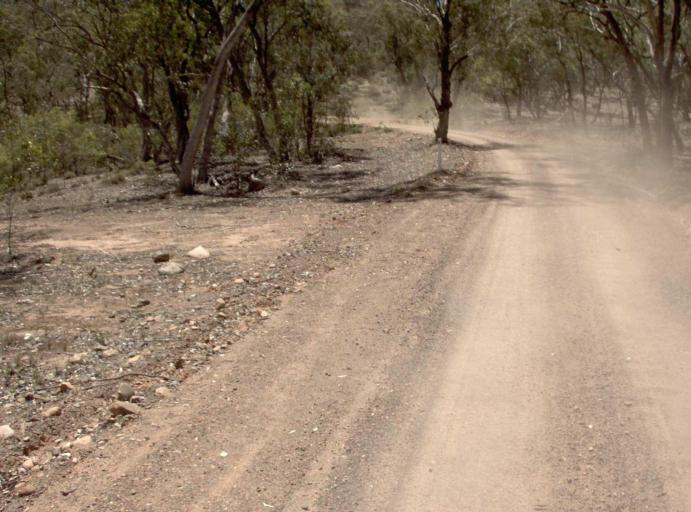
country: AU
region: New South Wales
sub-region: Snowy River
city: Jindabyne
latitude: -37.0900
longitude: 148.4097
